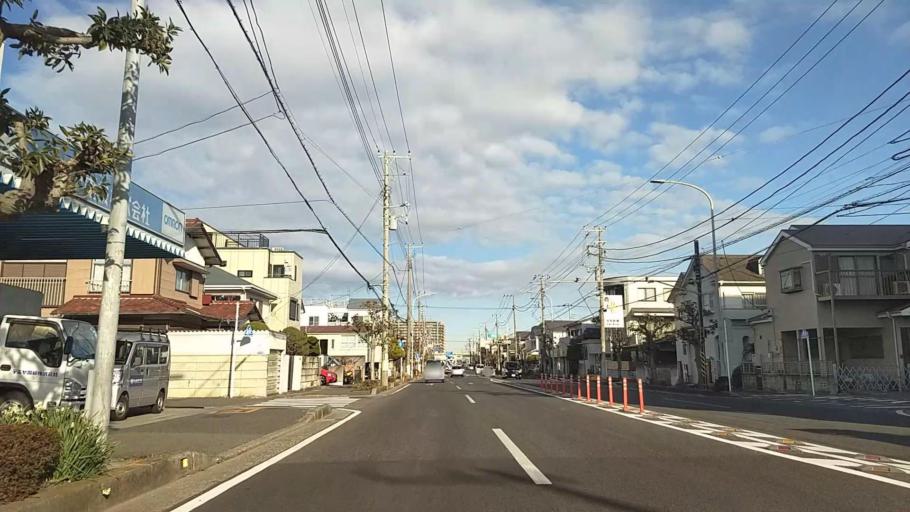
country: JP
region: Kanagawa
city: Hiratsuka
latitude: 35.3197
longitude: 139.3614
